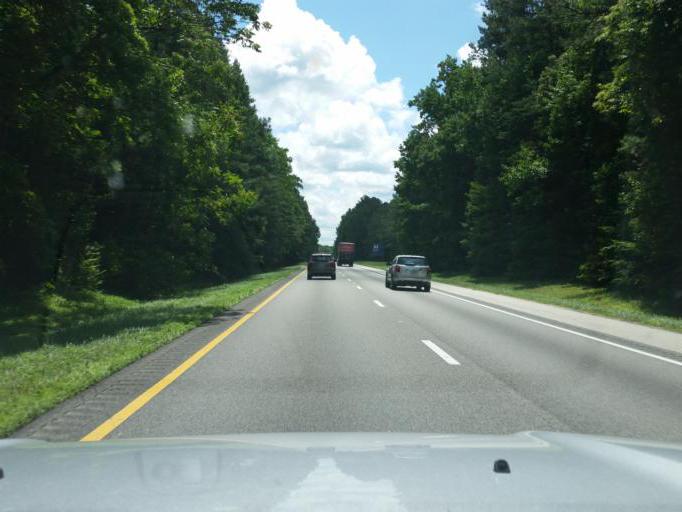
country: US
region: Virginia
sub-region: City of Williamsburg
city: Williamsburg
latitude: 37.3281
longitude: -76.7040
